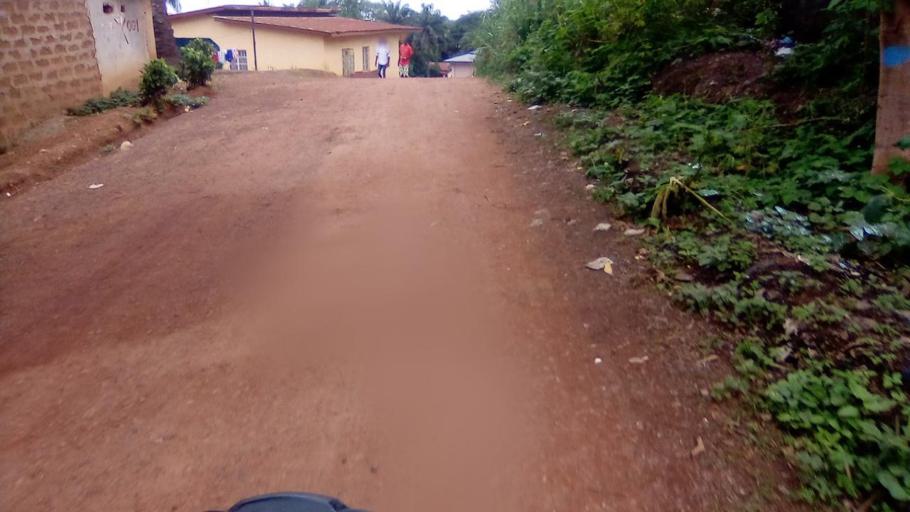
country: SL
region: Southern Province
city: Bo
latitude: 7.9573
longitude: -11.7259
